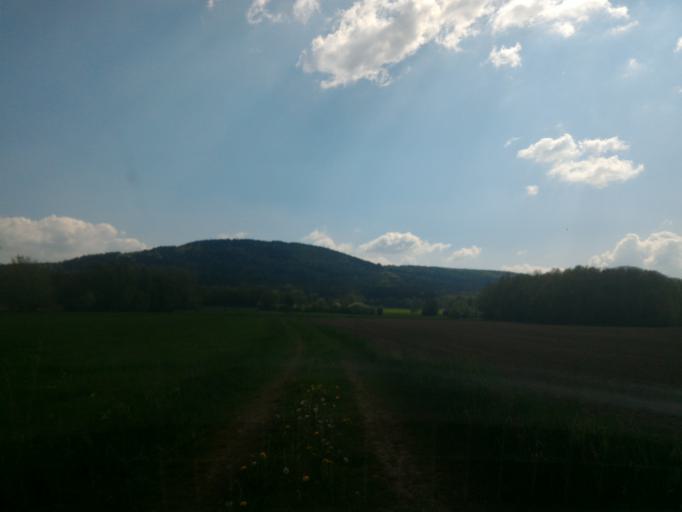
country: DE
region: Saxony
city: Grossschonau
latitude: 50.8730
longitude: 14.6802
